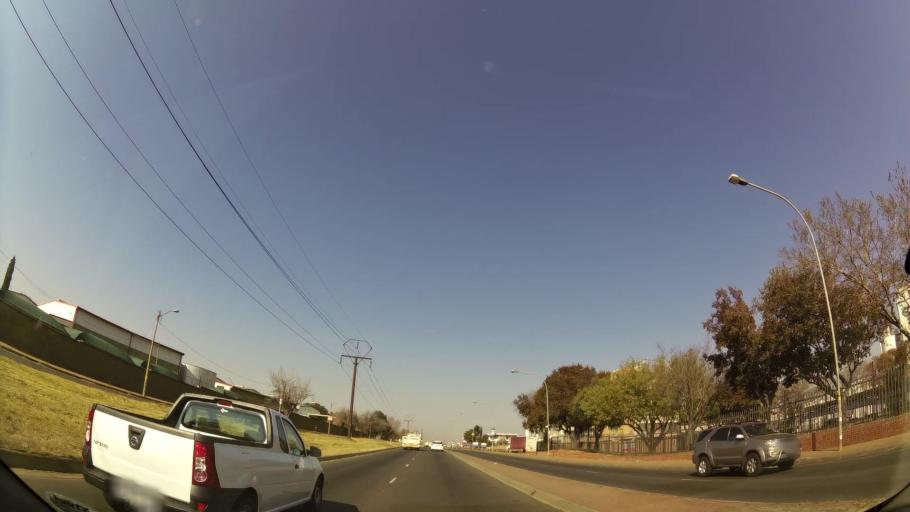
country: ZA
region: Gauteng
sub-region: City of Johannesburg Metropolitan Municipality
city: Modderfontein
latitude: -26.1379
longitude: 28.2019
